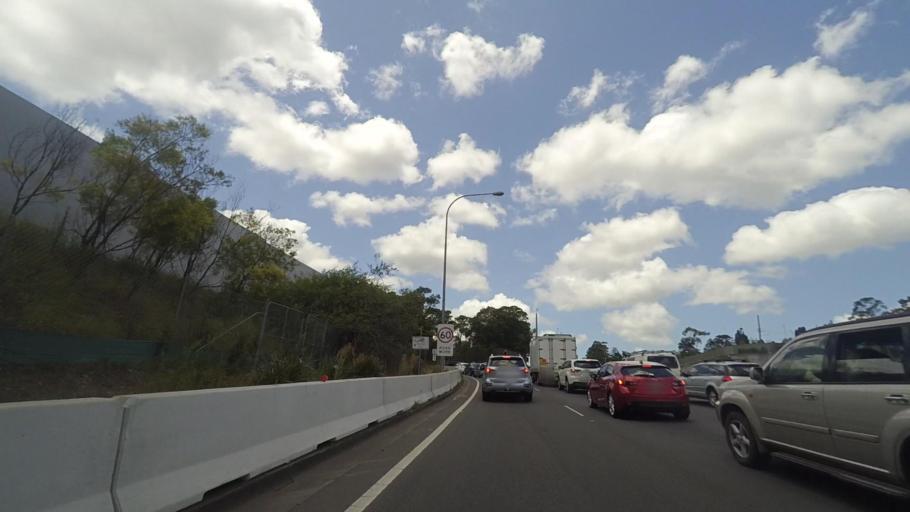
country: AU
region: New South Wales
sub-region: The Hills Shire
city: West Pennant
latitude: -33.7585
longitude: 151.0479
